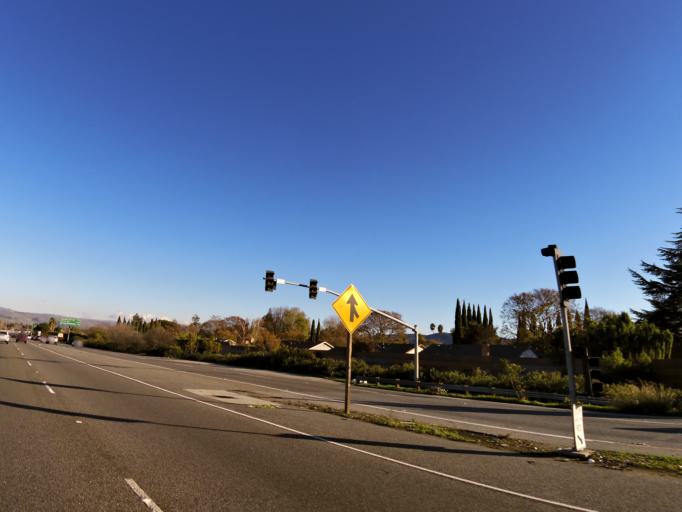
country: US
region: California
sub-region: Santa Clara County
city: Seven Trees
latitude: 37.2553
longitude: -121.8529
